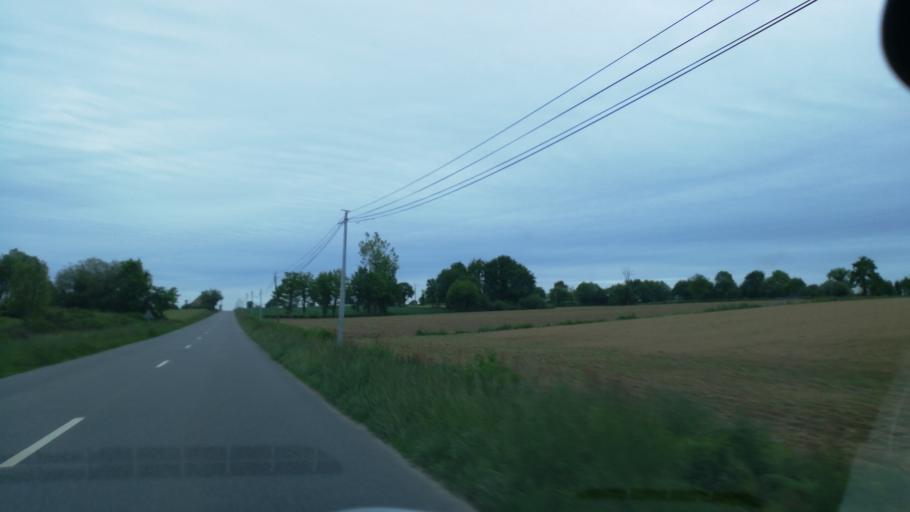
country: FR
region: Brittany
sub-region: Departement d'Ille-et-Vilaine
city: Irodouer
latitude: 48.2221
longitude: -1.9443
